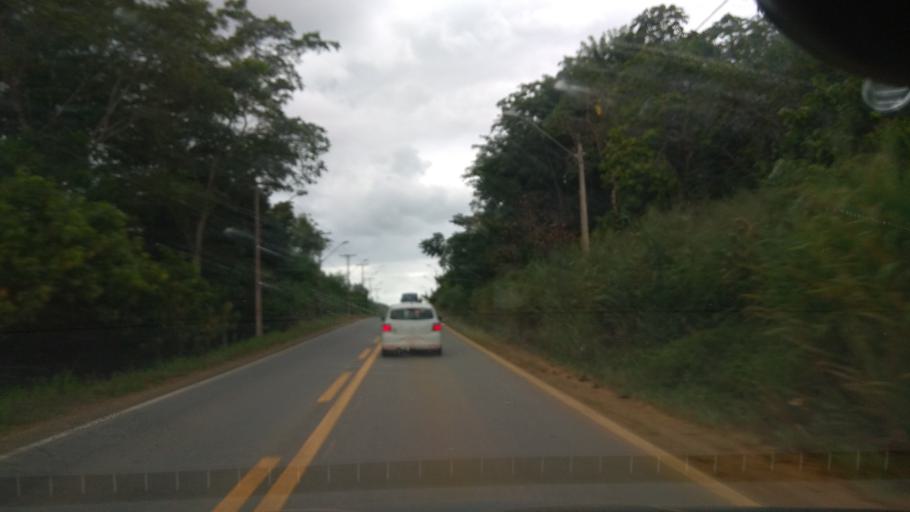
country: BR
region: Bahia
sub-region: Ubata
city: Ubata
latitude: -14.1956
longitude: -39.5450
